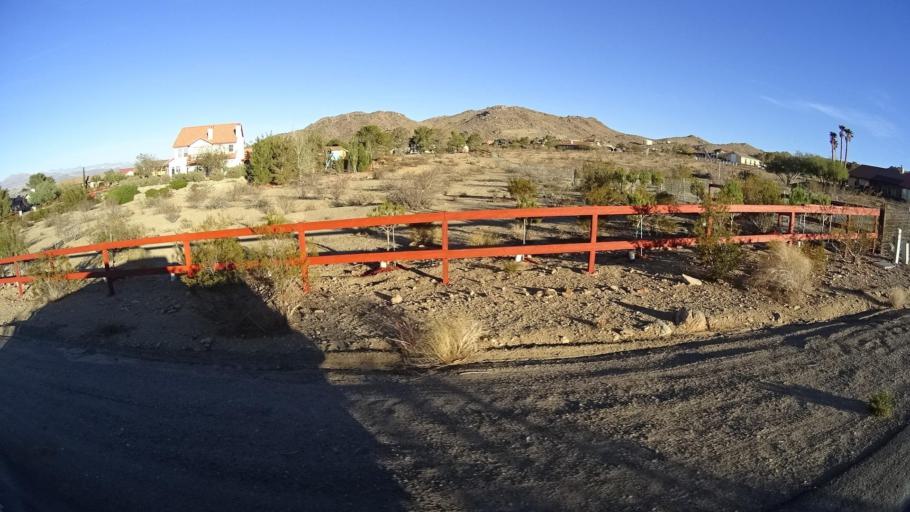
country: US
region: California
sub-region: Kern County
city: Ridgecrest
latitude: 35.5752
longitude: -117.6523
